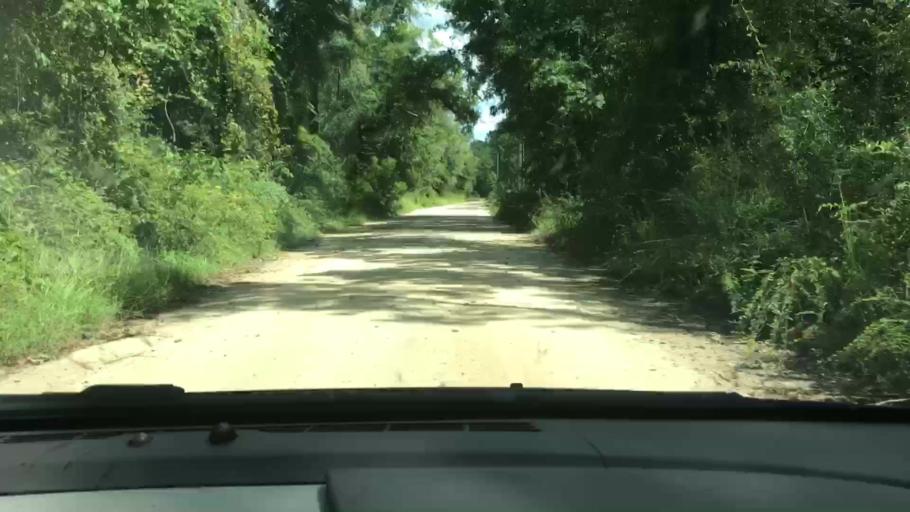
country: US
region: Georgia
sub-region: Clay County
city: Fort Gaines
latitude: 31.7335
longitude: -85.0921
